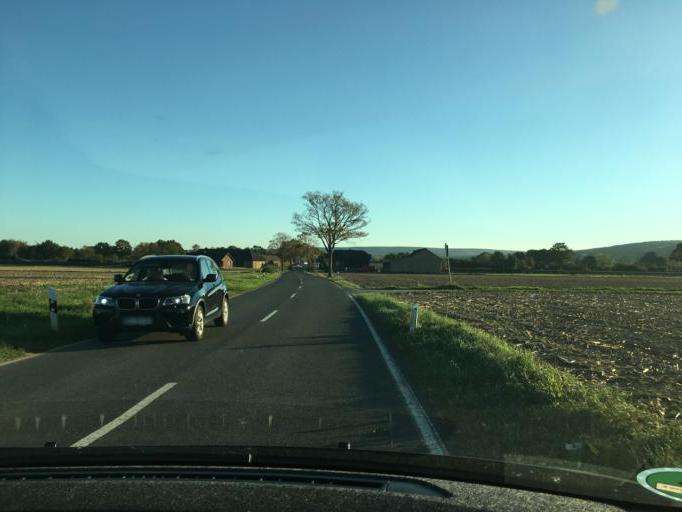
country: DE
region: North Rhine-Westphalia
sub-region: Regierungsbezirk Koln
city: Langerwehe
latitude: 50.8144
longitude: 6.3966
